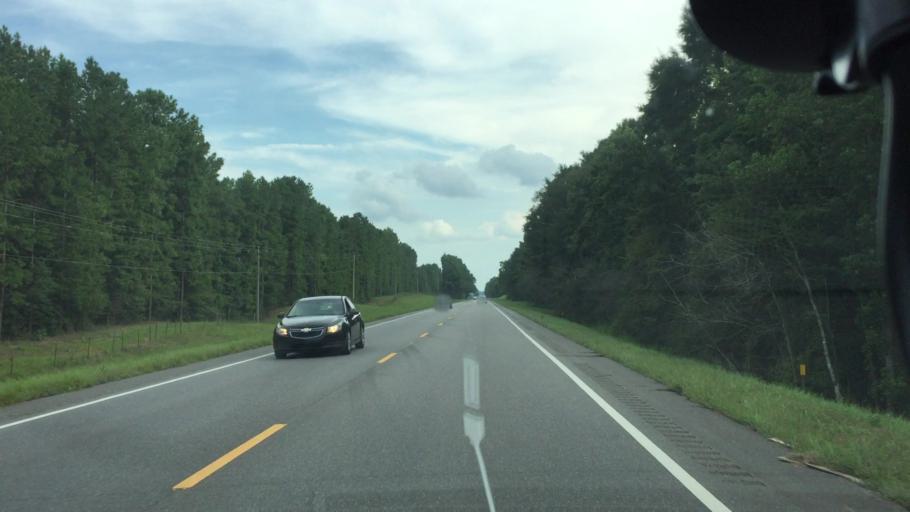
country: US
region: Alabama
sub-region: Coffee County
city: New Brockton
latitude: 31.5096
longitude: -85.9163
